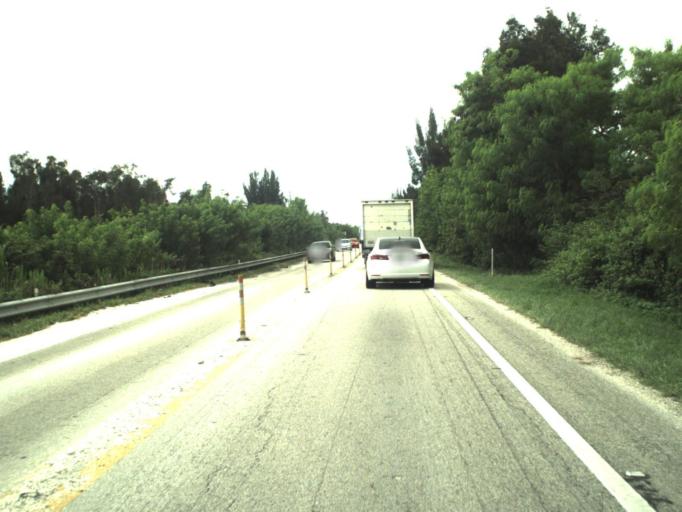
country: US
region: Florida
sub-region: Miami-Dade County
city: Kendall West
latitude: 25.7272
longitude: -80.4801
